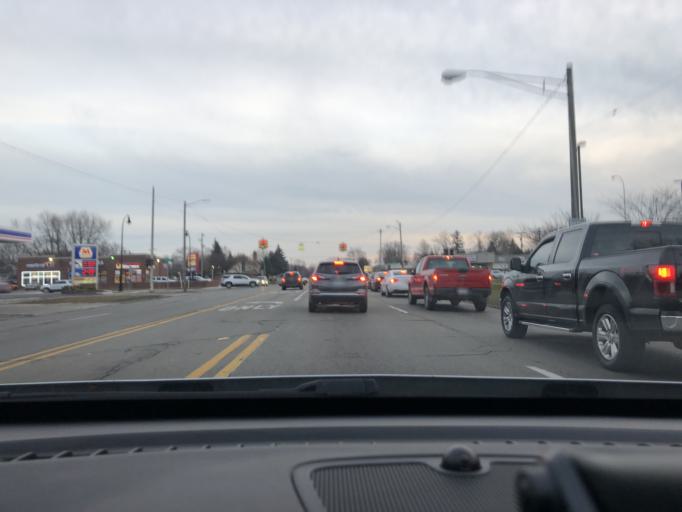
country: US
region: Michigan
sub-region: Wayne County
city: Allen Park
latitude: 42.2571
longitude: -83.2313
